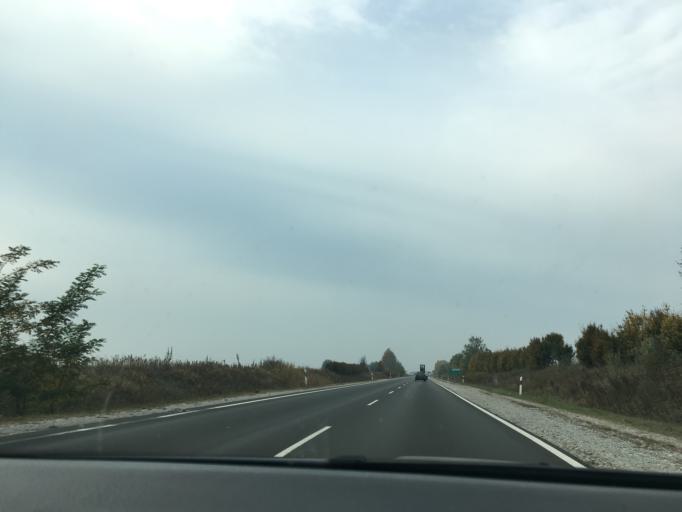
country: HU
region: Pest
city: Abony
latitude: 47.2185
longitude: 20.0266
